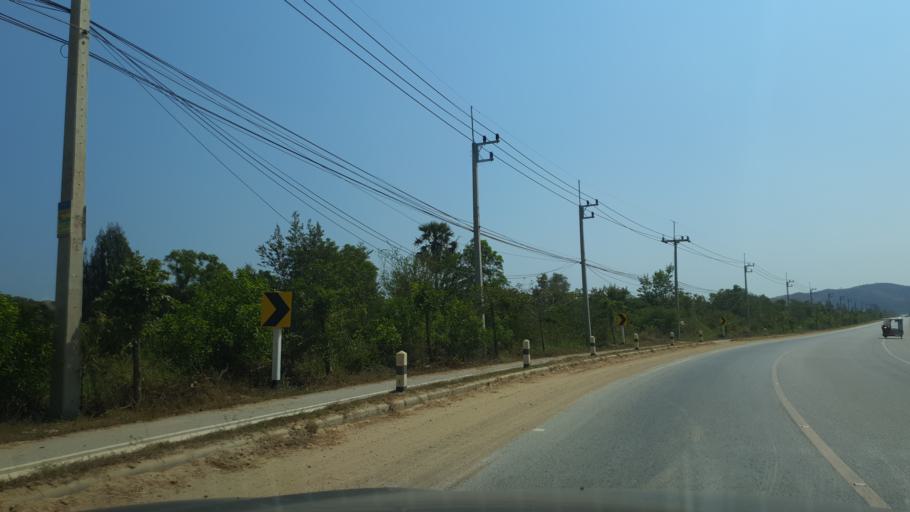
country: TH
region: Prachuap Khiri Khan
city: Pran Buri
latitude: 12.3357
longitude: 99.9547
